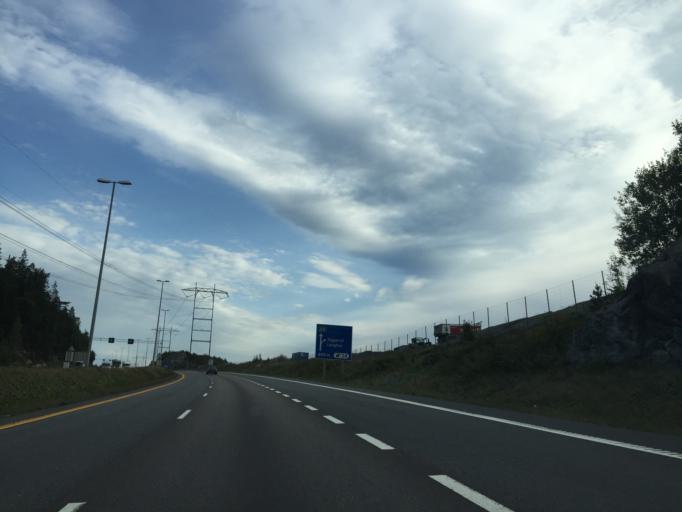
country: NO
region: Akershus
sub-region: Oppegard
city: Kolbotn
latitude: 59.7769
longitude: 10.8389
